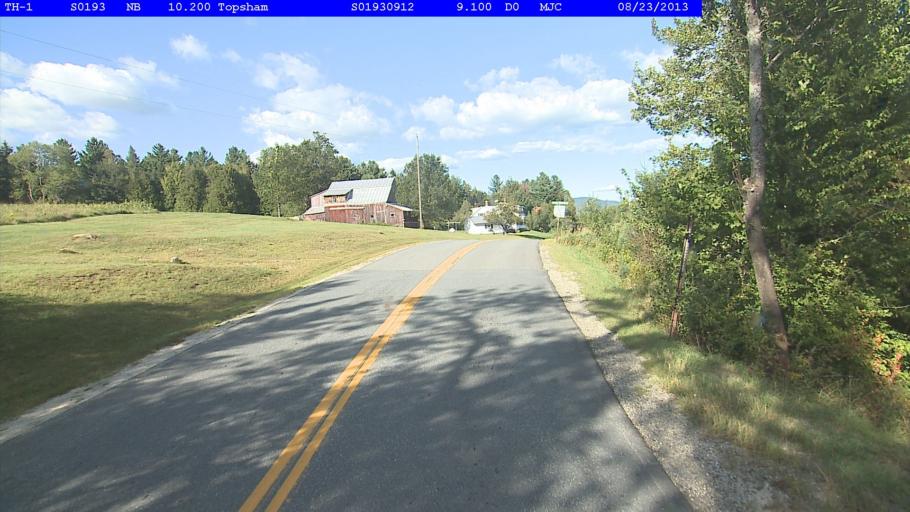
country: US
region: New Hampshire
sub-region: Grafton County
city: Woodsville
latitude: 44.1891
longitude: -72.2212
